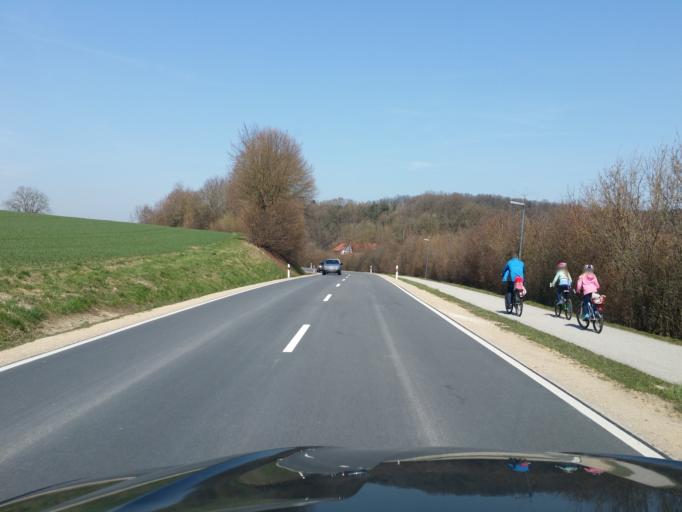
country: DE
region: Bavaria
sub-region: Upper Bavaria
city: Langenpreising
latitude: 48.4558
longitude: 12.0219
